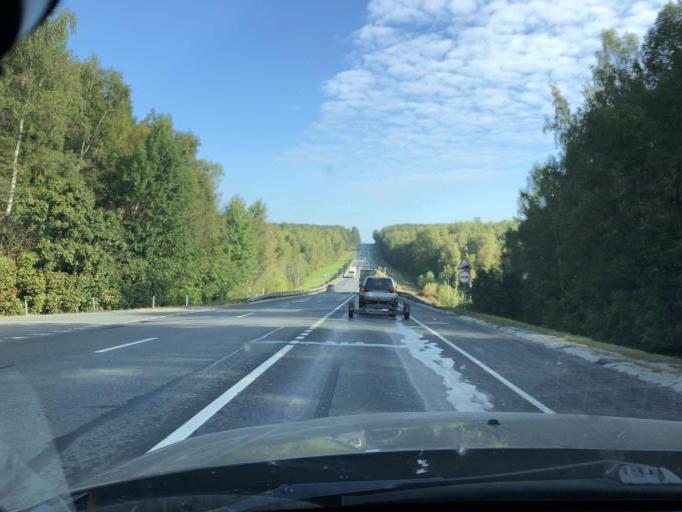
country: RU
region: Tula
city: Barsuki
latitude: 54.2736
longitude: 37.5351
